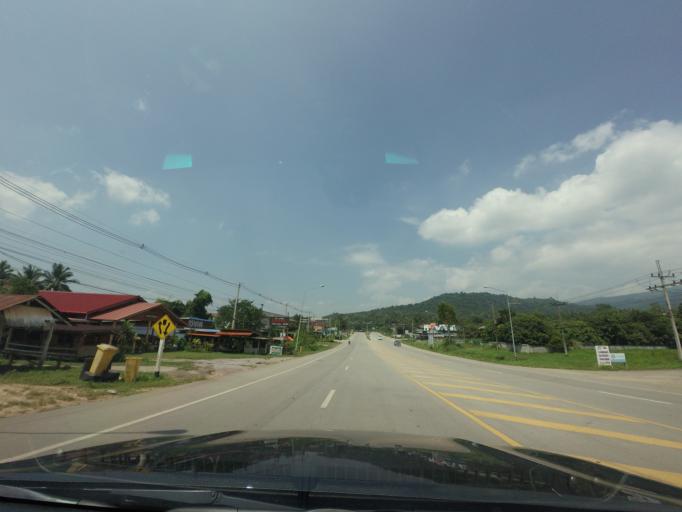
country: TH
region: Loei
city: Phu Ruea
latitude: 17.4565
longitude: 101.3759
